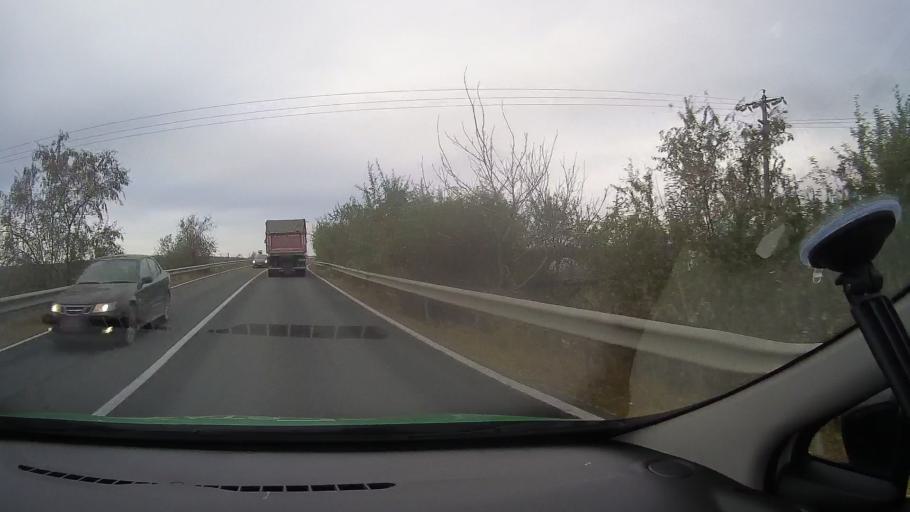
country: RO
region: Constanta
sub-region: Comuna Poarta Alba
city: Poarta Alba
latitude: 44.2145
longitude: 28.3919
